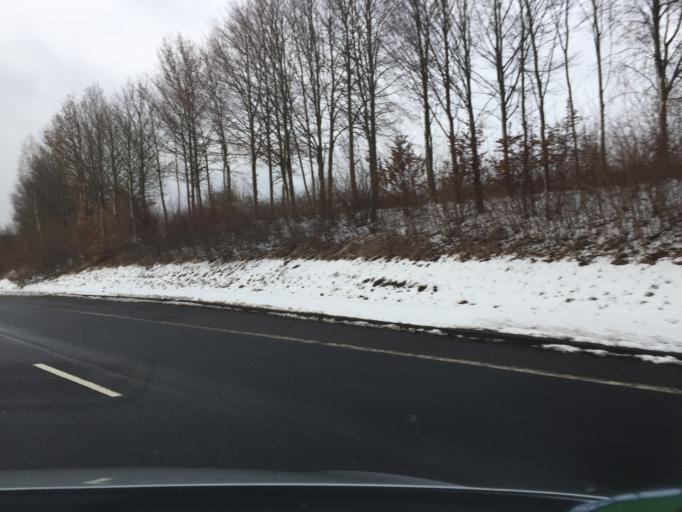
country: DE
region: Bavaria
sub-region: Regierungsbezirk Unterfranken
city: Hosbach
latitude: 50.0345
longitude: 9.2008
